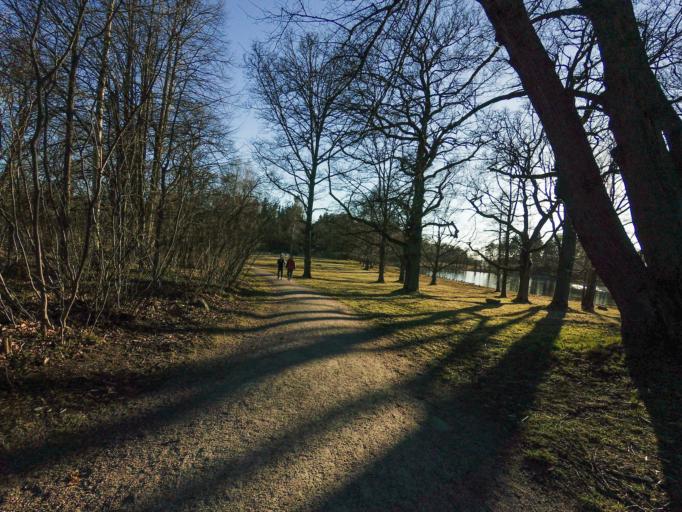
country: FI
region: Uusimaa
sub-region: Helsinki
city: Helsinki
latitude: 60.1791
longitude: 25.0307
